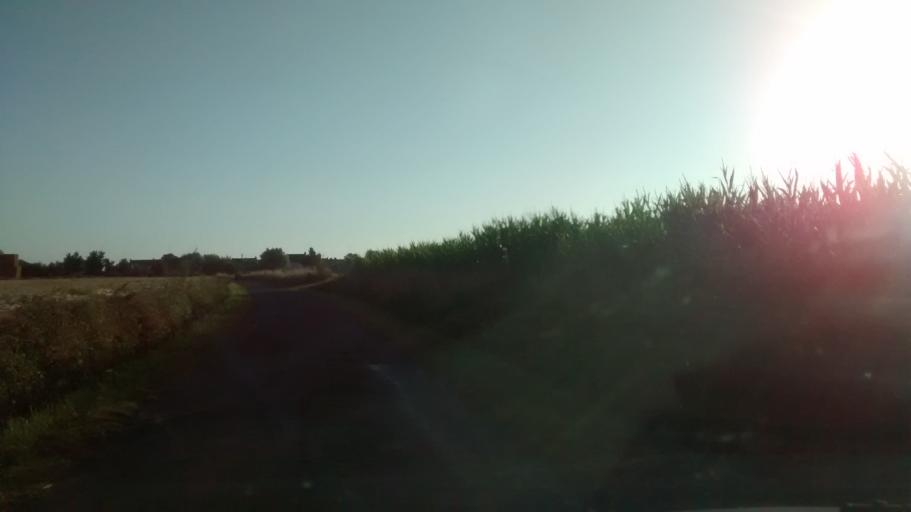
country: FR
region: Brittany
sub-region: Departement d'Ille-et-Vilaine
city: La Fresnais
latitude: 48.6103
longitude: -1.8484
